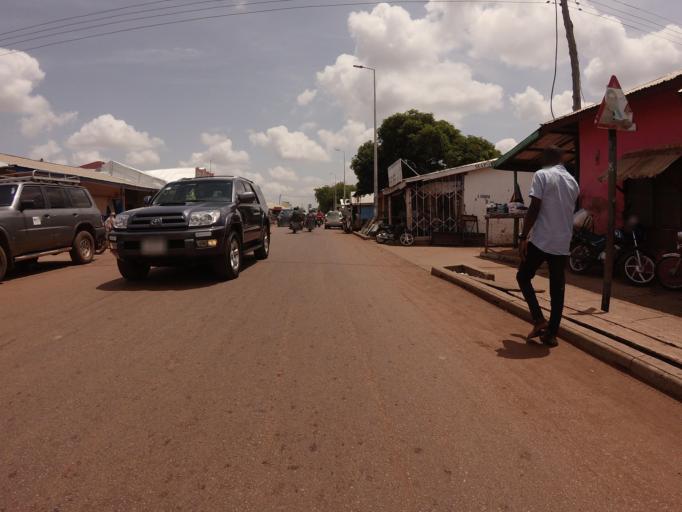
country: GH
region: Northern
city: Tamale
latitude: 9.4015
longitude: -0.8420
